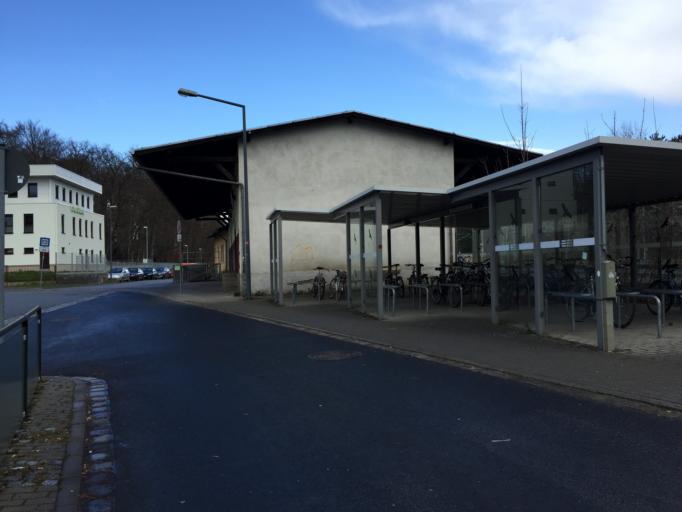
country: DE
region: Saxony
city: Albertstadt
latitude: 51.1150
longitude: 13.7889
